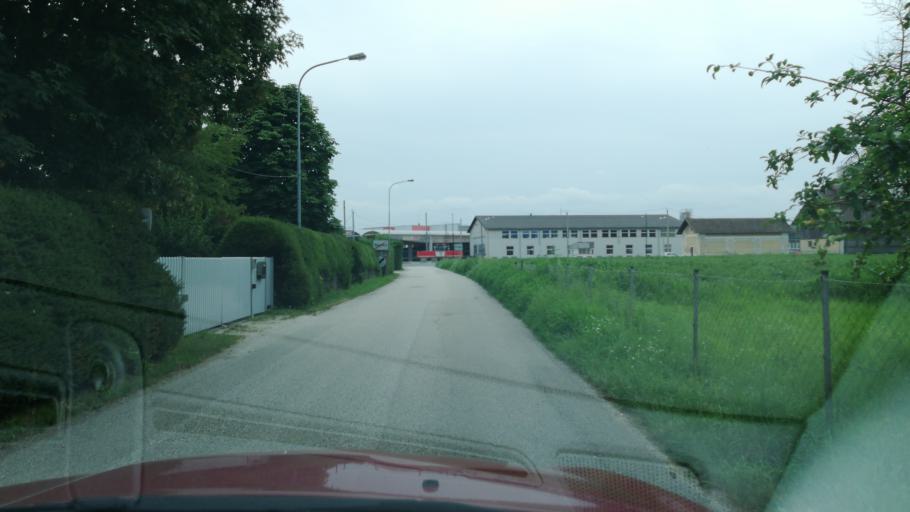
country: AT
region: Upper Austria
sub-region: Politischer Bezirk Urfahr-Umgebung
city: Feldkirchen an der Donau
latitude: 48.3035
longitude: 14.0138
